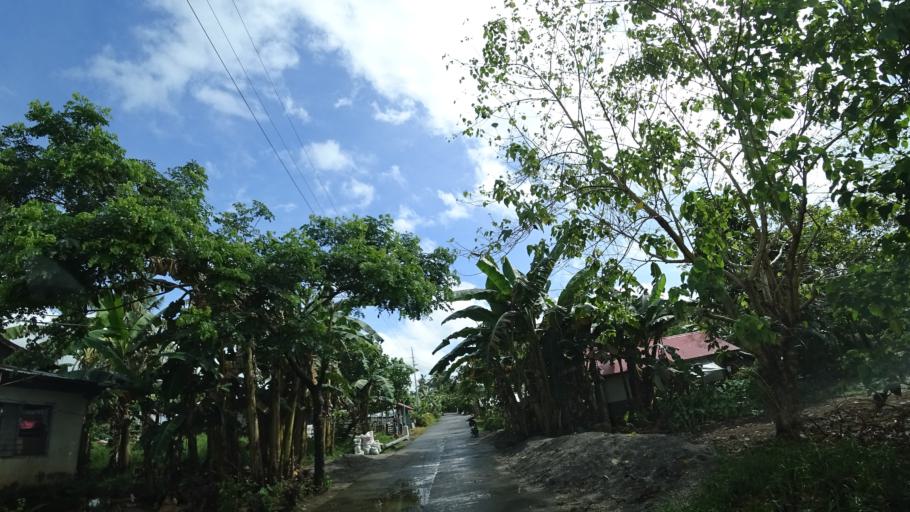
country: PH
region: Eastern Visayas
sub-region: Province of Leyte
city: Cabacungan
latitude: 10.9176
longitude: 124.9763
